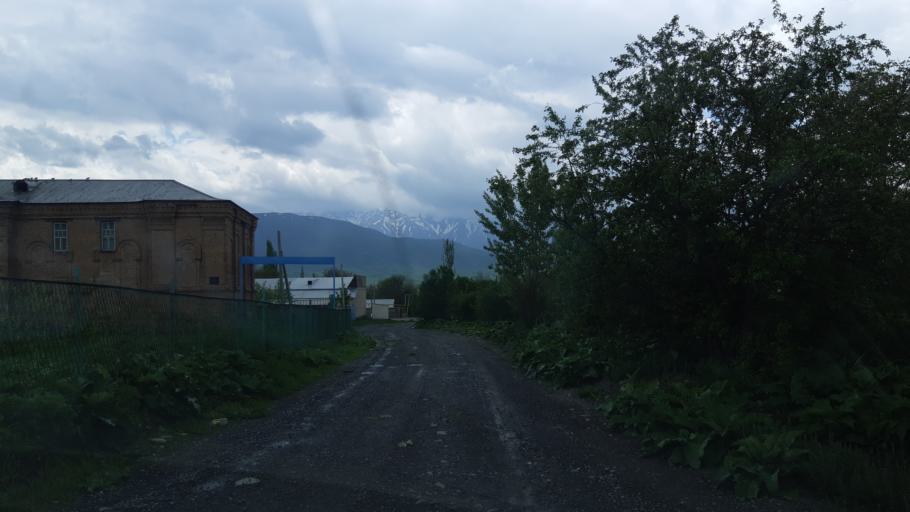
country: KZ
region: Ongtustik Qazaqstan
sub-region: Tulkibas Audany
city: Zhabagly
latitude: 42.5133
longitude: 70.5623
